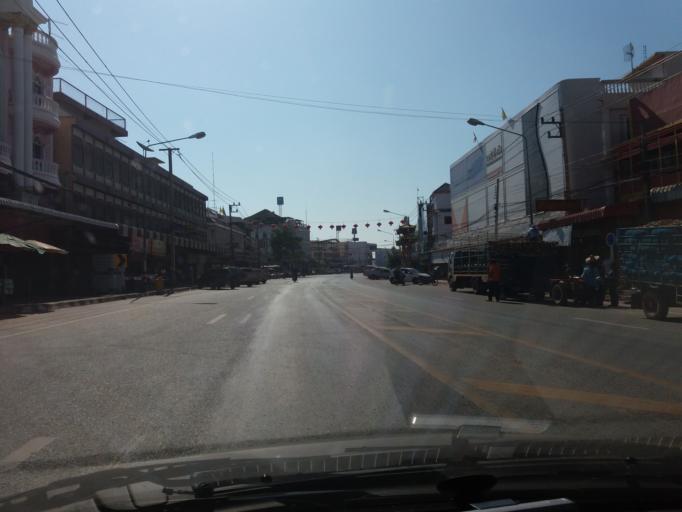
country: TH
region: Kamphaeng Phet
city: Khlong Khlung
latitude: 16.2365
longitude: 99.7312
